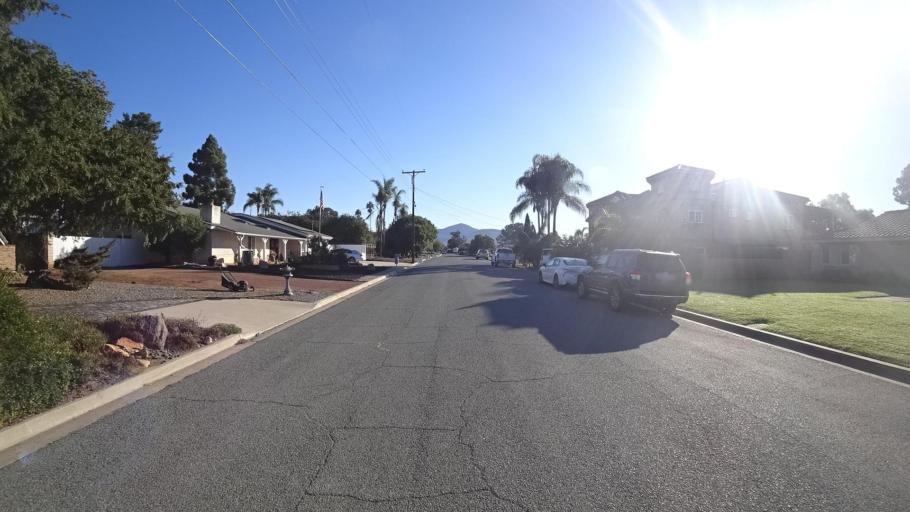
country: US
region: California
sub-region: San Diego County
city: Bonita
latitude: 32.6734
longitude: -117.0282
